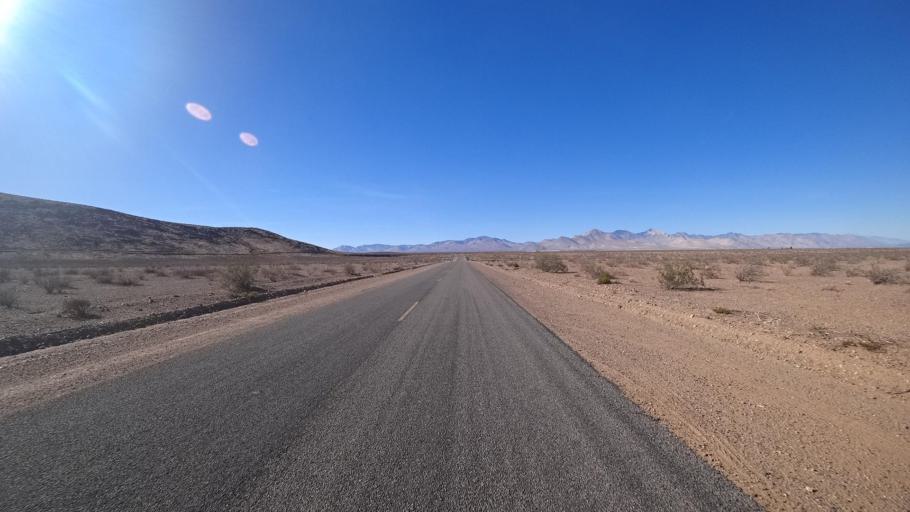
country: US
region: California
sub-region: Kern County
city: China Lake Acres
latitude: 35.5594
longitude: -117.7681
